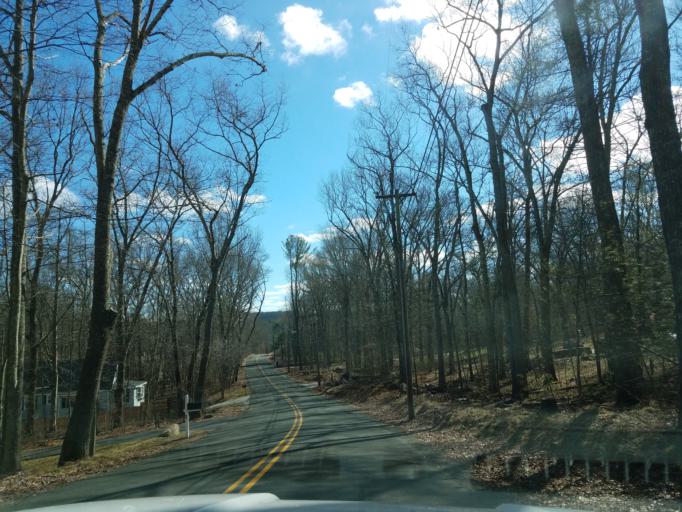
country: US
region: Massachusetts
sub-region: Worcester County
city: Webster
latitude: 42.0155
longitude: -71.8729
